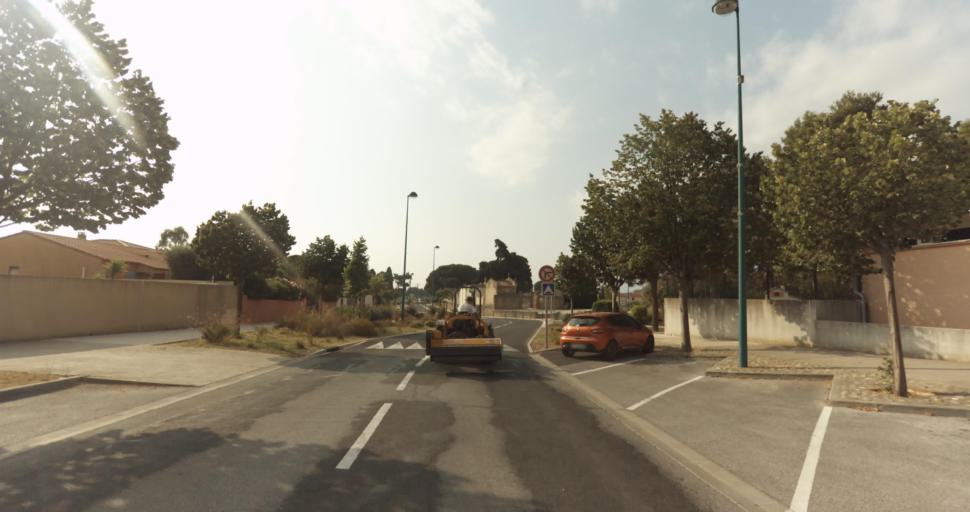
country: FR
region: Languedoc-Roussillon
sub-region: Departement des Pyrenees-Orientales
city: Corneilla-del-Vercol
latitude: 42.6254
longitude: 2.9531
